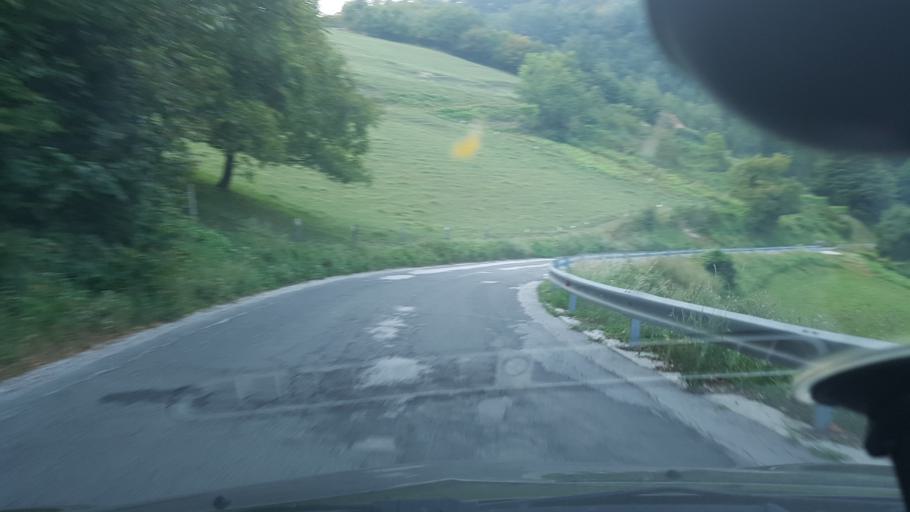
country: SI
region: Kozje
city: Kozje
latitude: 46.0389
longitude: 15.5759
